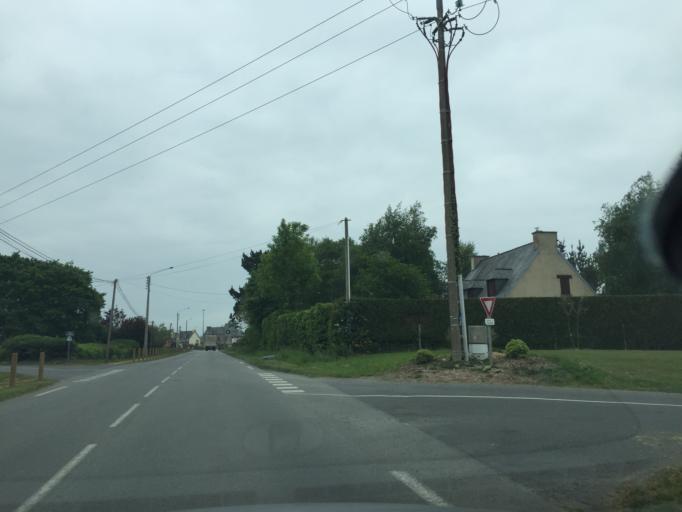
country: FR
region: Brittany
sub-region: Departement des Cotes-d'Armor
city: Crehen
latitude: 48.5804
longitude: -2.2347
